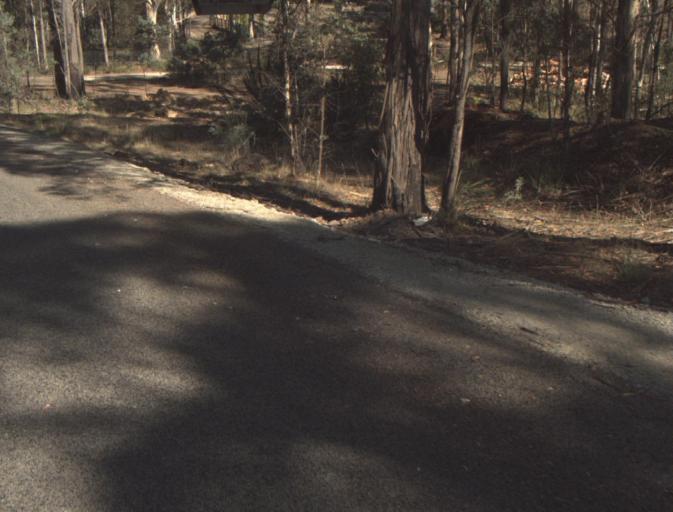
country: AU
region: Tasmania
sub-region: Launceston
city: Mayfield
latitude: -41.2765
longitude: 147.1086
